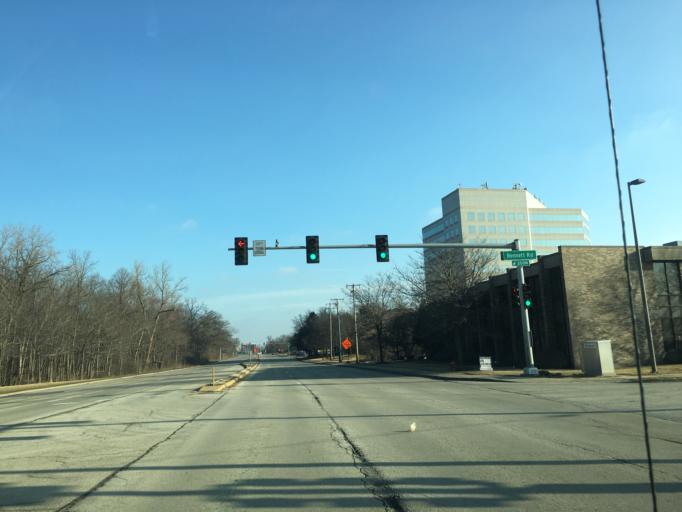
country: US
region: Illinois
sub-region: Cook County
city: Elk Grove Village
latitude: 42.0309
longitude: -87.9861
